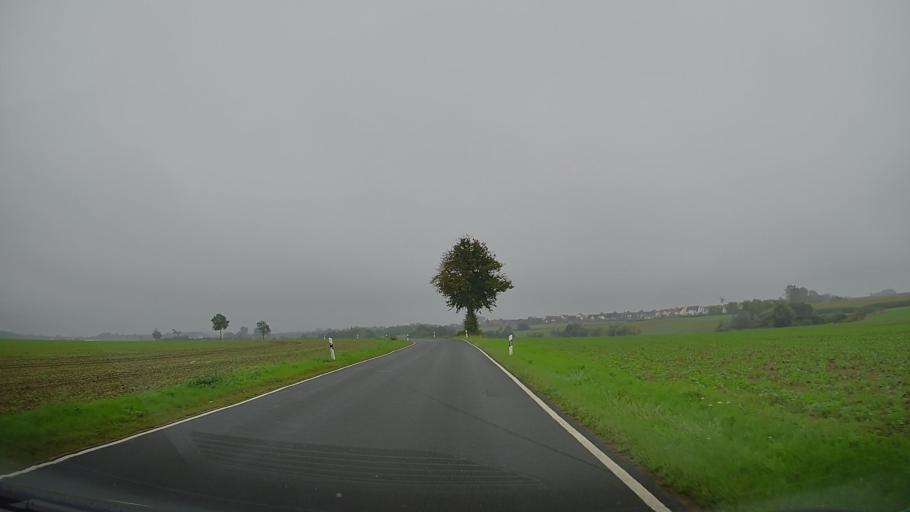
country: DE
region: Mecklenburg-Vorpommern
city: Wismar
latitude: 53.9152
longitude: 11.3949
